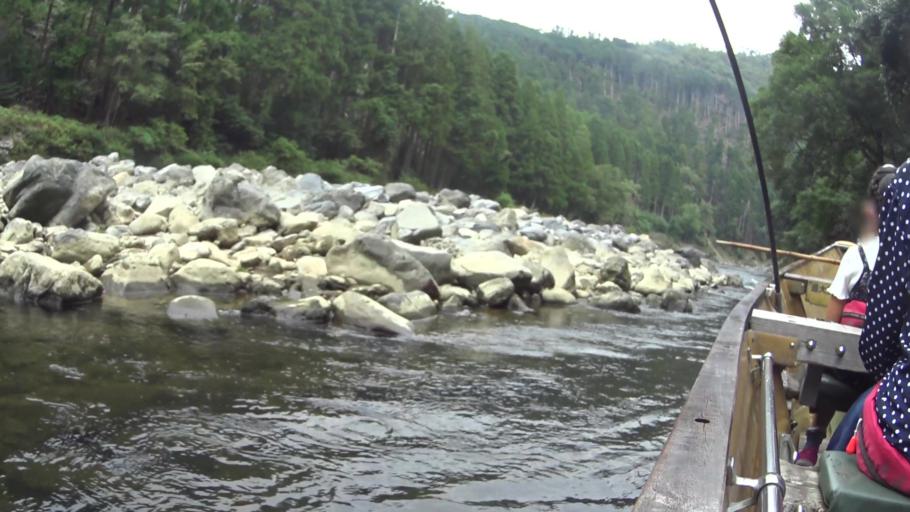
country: JP
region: Kyoto
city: Kameoka
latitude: 35.0248
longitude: 135.6283
